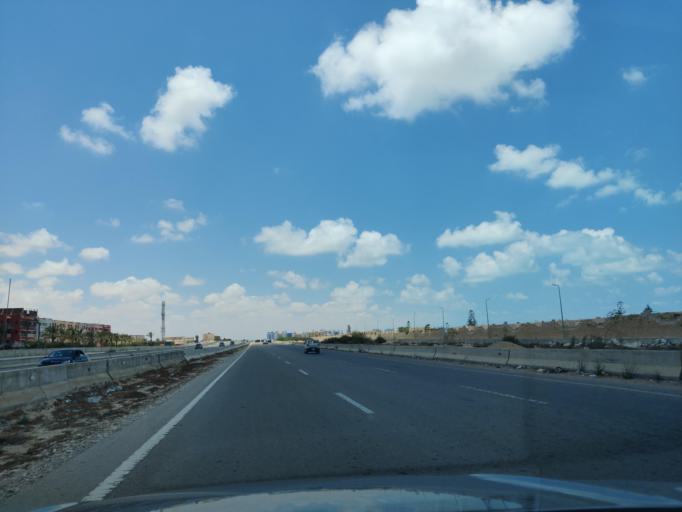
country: EG
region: Muhafazat Matruh
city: Al `Alamayn
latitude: 30.8186
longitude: 29.0250
